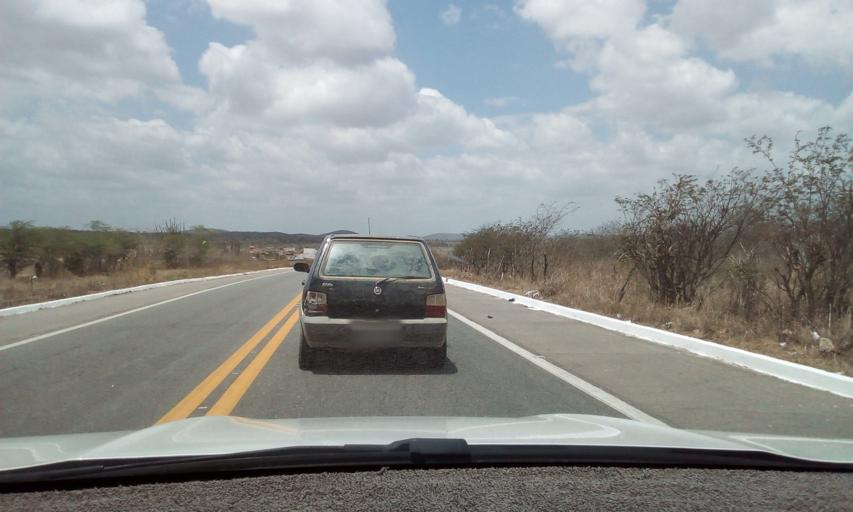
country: BR
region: Pernambuco
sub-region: Taquaritinga Do Norte
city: Taquaritinga do Norte
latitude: -7.7323
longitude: -36.0761
